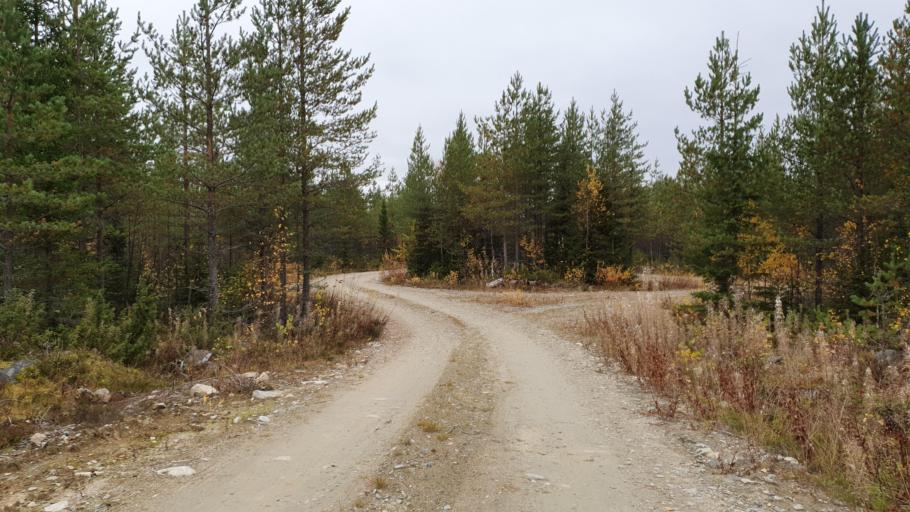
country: FI
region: Kainuu
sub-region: Kehys-Kainuu
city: Kuhmo
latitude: 64.4479
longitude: 29.6173
